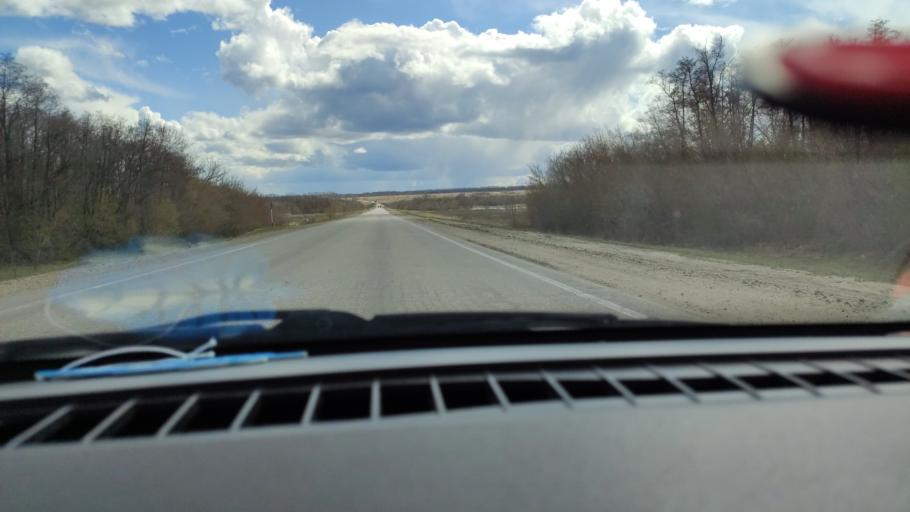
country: RU
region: Samara
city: Varlamovo
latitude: 53.1410
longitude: 48.2856
